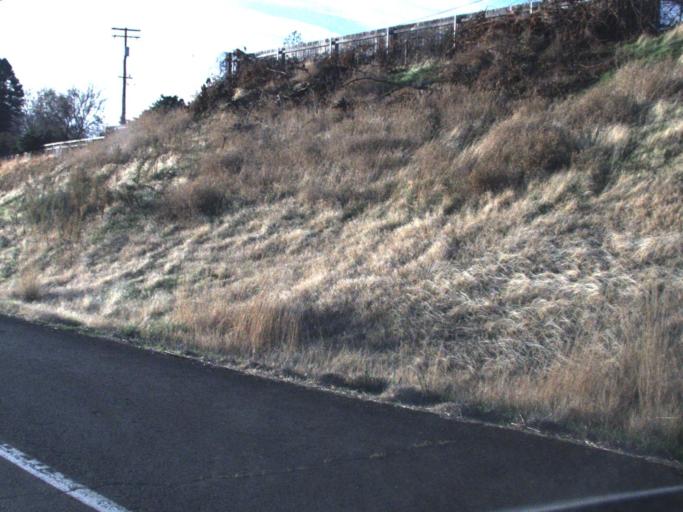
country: US
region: Washington
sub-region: Walla Walla County
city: Walla Walla East
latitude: 46.0818
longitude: -118.2999
